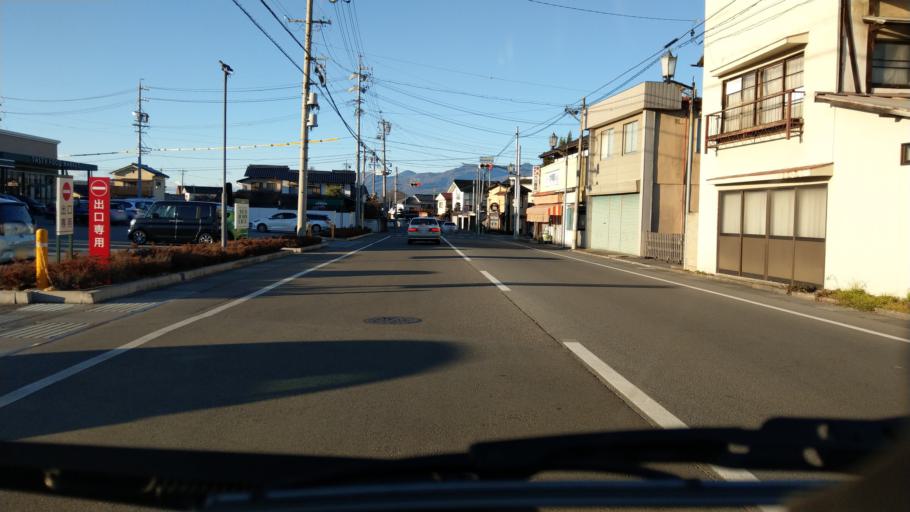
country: JP
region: Nagano
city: Saku
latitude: 36.2334
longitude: 138.4750
